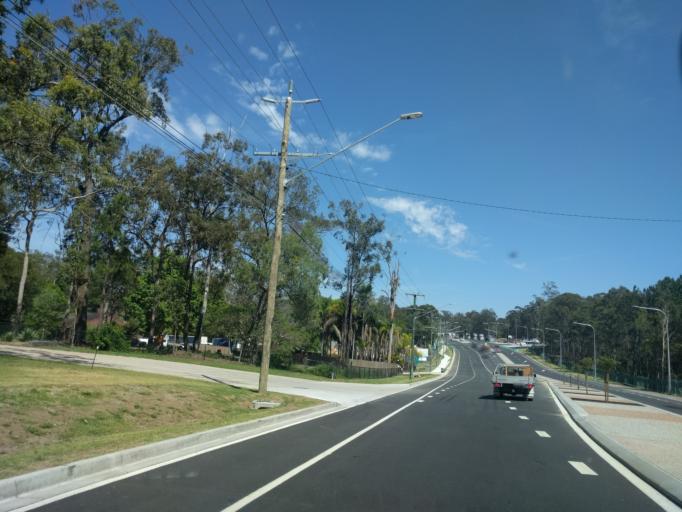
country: AU
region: Queensland
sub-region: Brisbane
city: Forest Lake
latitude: -27.6500
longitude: 152.9864
